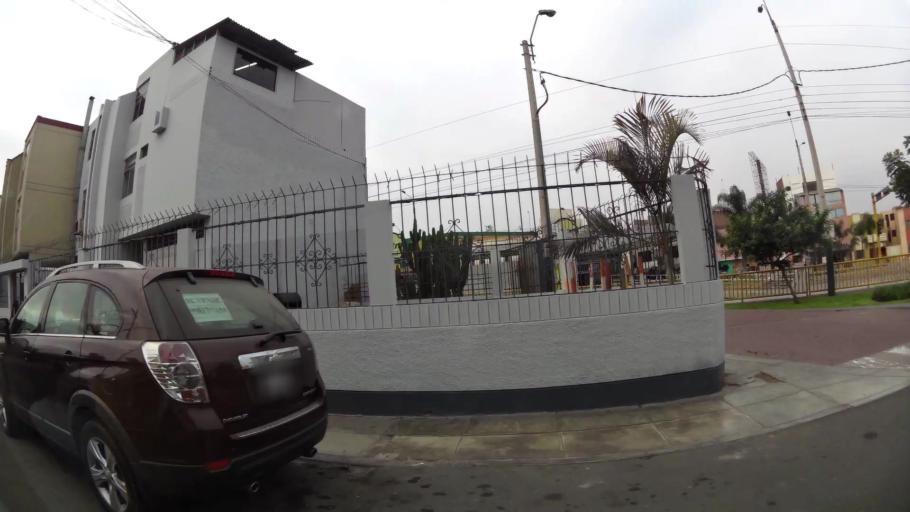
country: PE
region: Lima
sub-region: Lima
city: Surco
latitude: -12.1414
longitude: -77.0180
